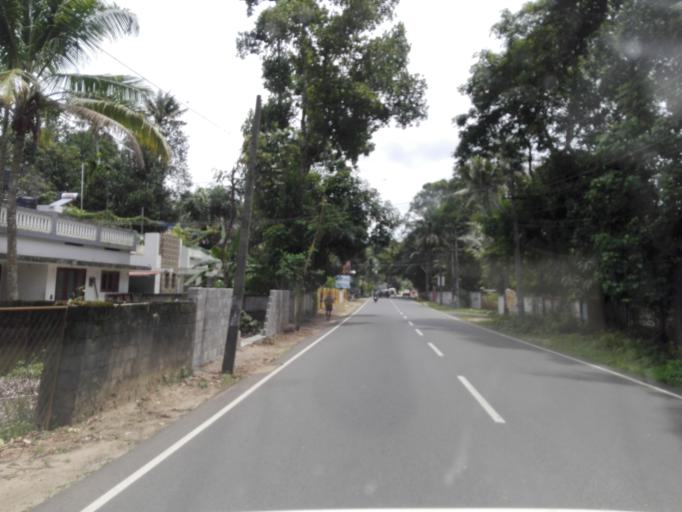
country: IN
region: Kerala
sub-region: Alappuzha
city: Arukutti
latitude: 9.8595
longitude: 76.3828
